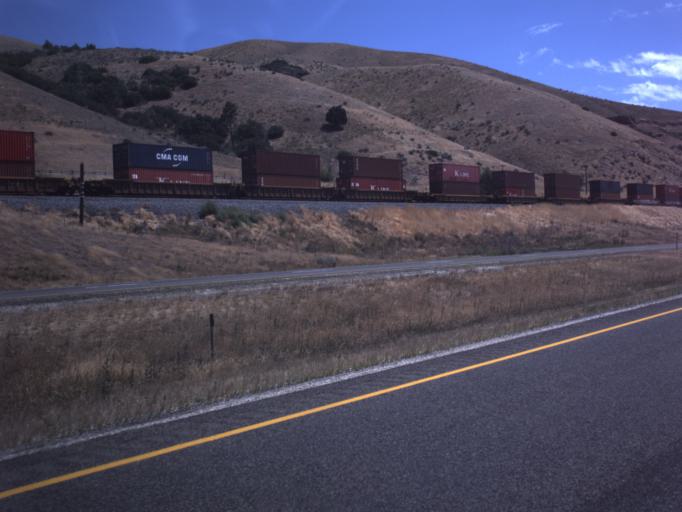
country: US
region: Utah
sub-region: Summit County
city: Coalville
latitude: 41.0029
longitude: -111.4720
